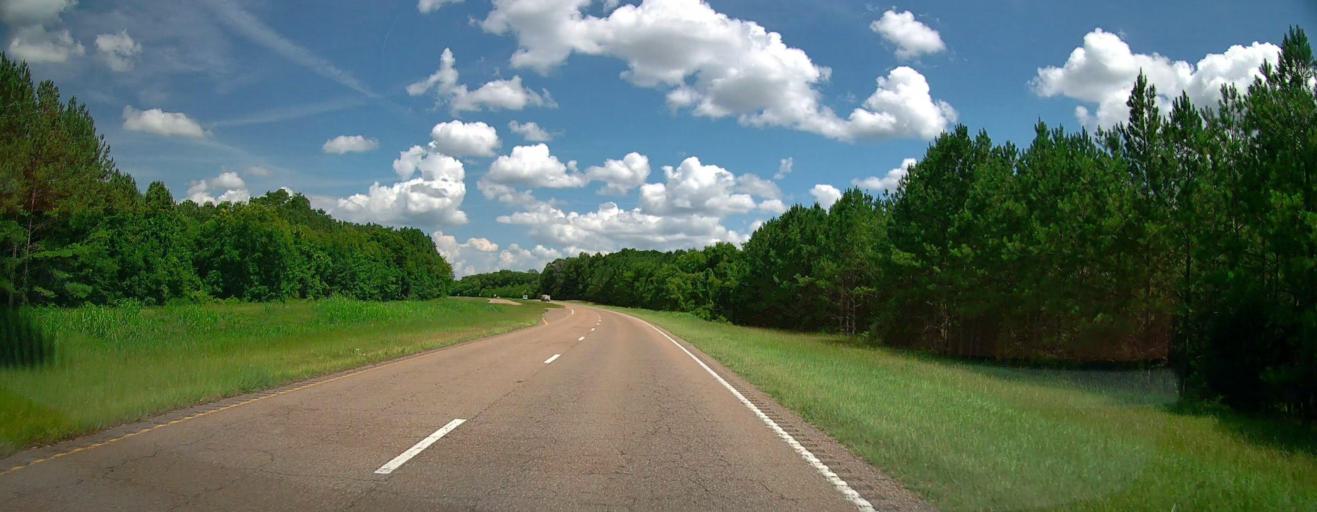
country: US
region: Mississippi
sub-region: Monroe County
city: Aberdeen
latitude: 33.8180
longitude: -88.5798
